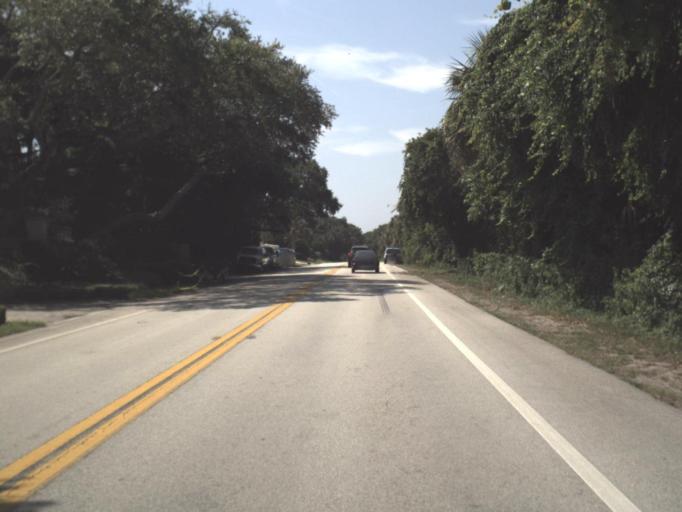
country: US
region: Florida
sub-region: Saint Johns County
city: Palm Valley
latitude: 30.1482
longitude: -81.3537
